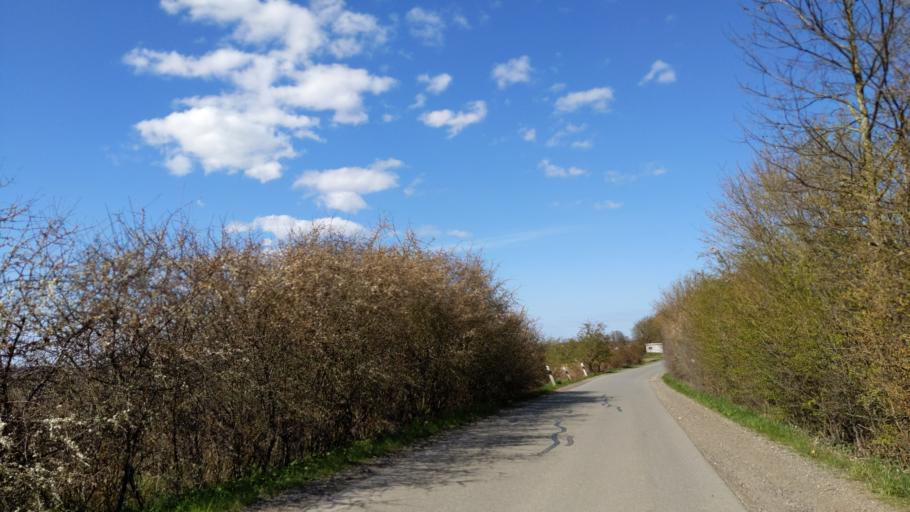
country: DE
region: Schleswig-Holstein
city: Kasseedorf
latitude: 54.1266
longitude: 10.6879
